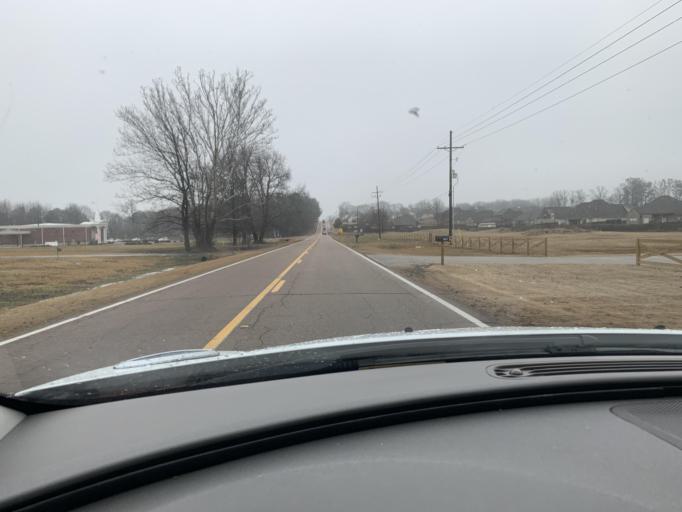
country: US
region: Mississippi
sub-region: De Soto County
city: Hernando
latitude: 34.8494
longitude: -89.9951
